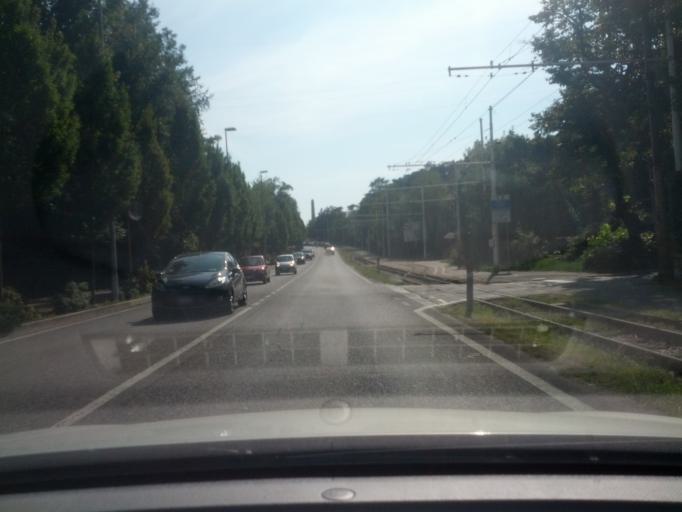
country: IT
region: Friuli Venezia Giulia
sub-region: Provincia di Trieste
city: Villa Opicina
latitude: 45.6823
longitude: 13.7827
